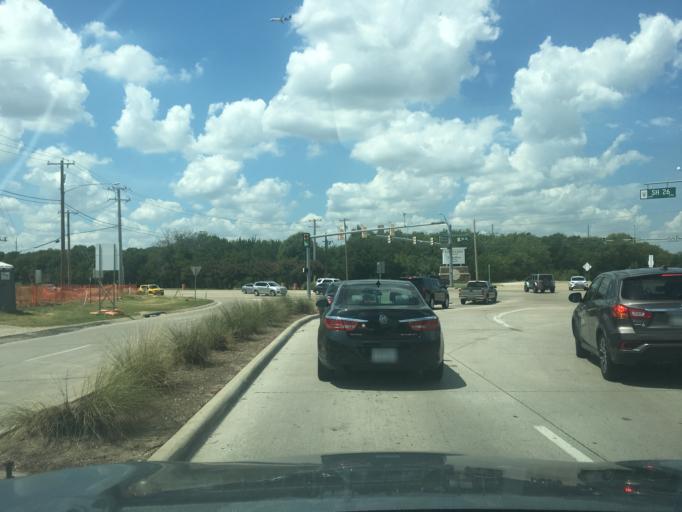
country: US
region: Texas
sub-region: Dallas County
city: Coppell
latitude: 32.9553
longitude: -97.0474
